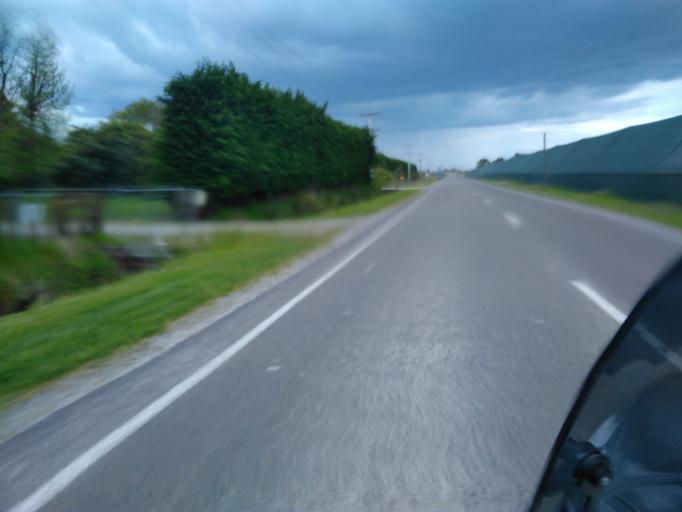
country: NZ
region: Gisborne
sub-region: Gisborne District
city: Gisborne
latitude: -38.6491
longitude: 177.9099
